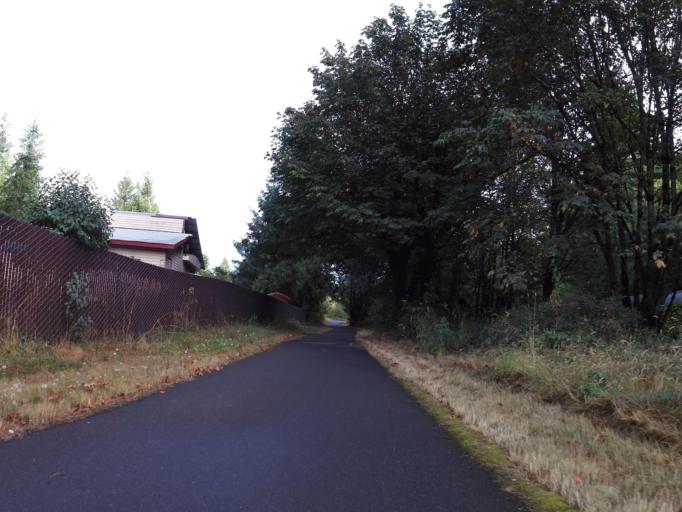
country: US
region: Washington
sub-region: Thurston County
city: Tenino
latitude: 46.9207
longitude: -122.8031
